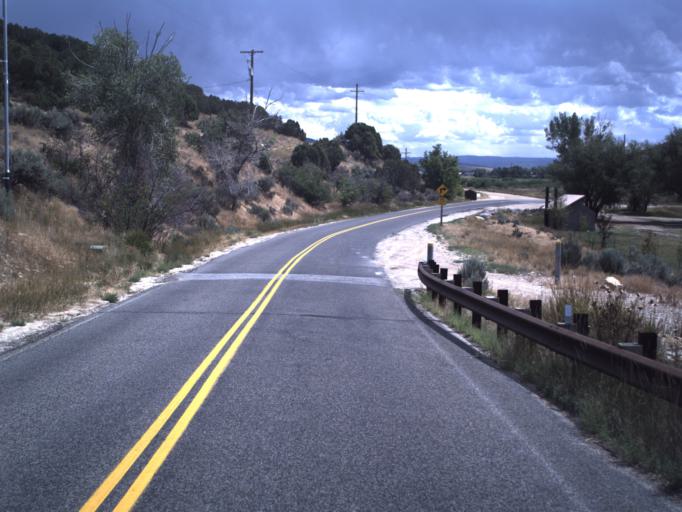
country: US
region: Utah
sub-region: Summit County
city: Oakley
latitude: 40.7551
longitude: -111.3722
